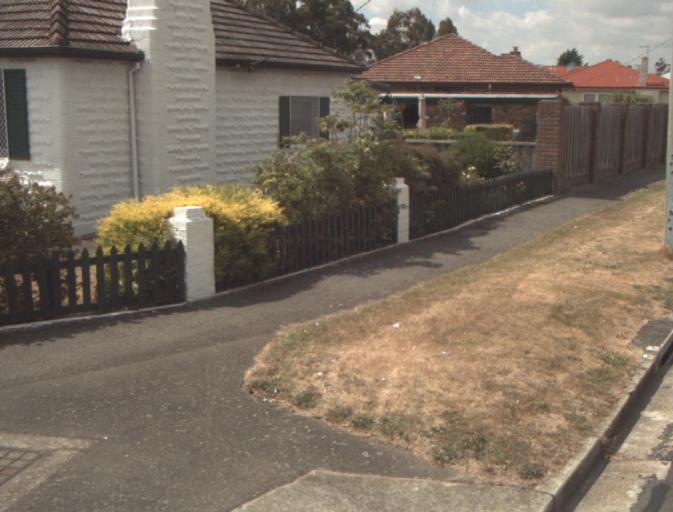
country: AU
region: Tasmania
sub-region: Launceston
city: Summerhill
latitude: -41.4692
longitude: 147.1587
